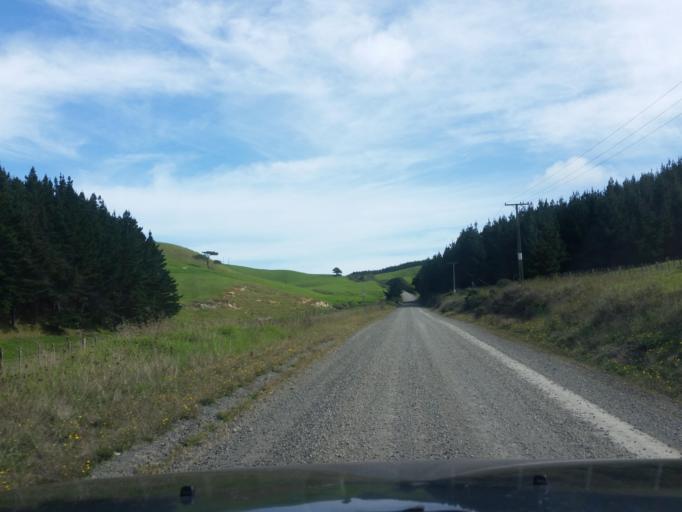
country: NZ
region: Northland
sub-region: Kaipara District
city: Dargaville
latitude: -35.9340
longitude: 173.7673
